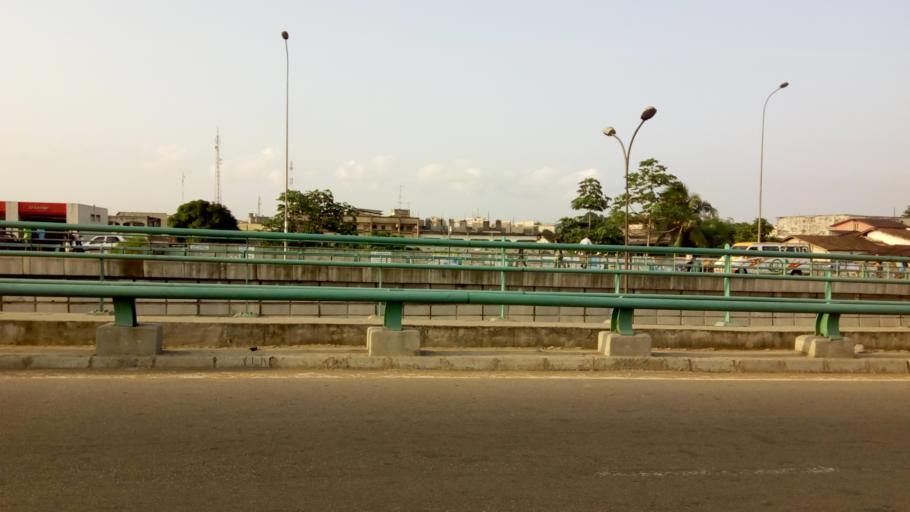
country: CI
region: Lagunes
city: Abidjan
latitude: 5.3537
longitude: -3.9778
